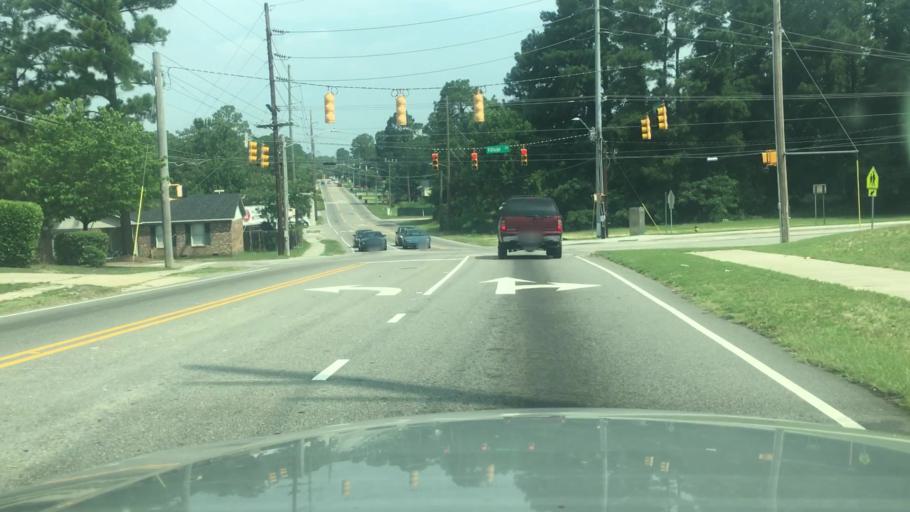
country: US
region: North Carolina
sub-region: Cumberland County
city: Hope Mills
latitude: 35.0254
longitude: -78.9423
